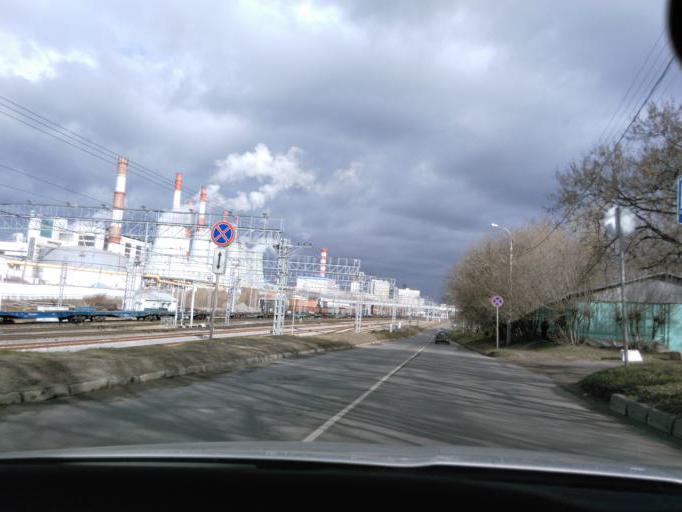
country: RU
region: Moscow
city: Novyye Cheremushki
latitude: 55.6962
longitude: 37.5966
